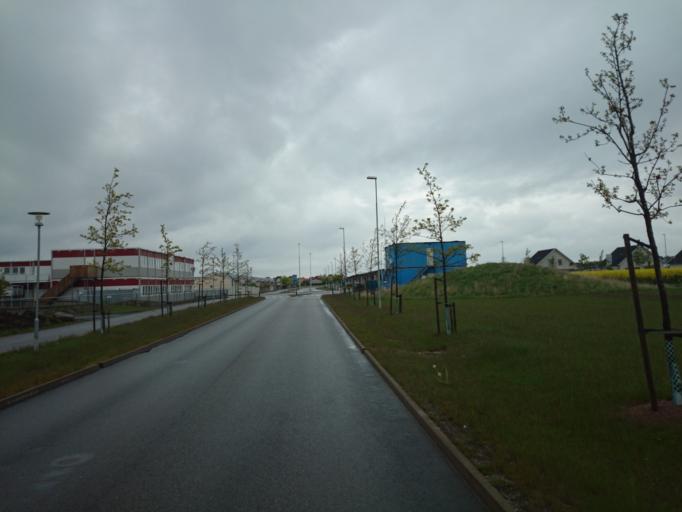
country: SE
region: Skane
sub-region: Malmo
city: Bunkeflostrand
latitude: 55.5486
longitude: 12.9285
